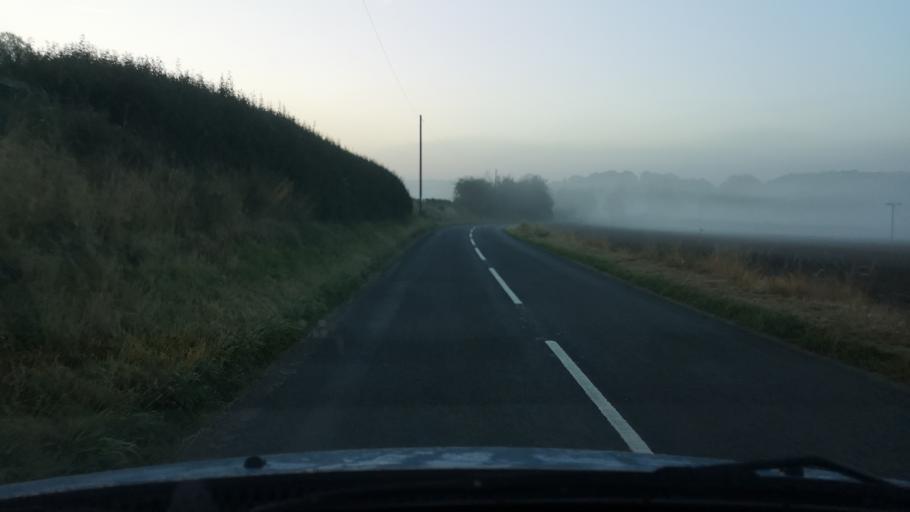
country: GB
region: England
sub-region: City and Borough of Wakefield
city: Darrington
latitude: 53.6535
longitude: -1.2695
